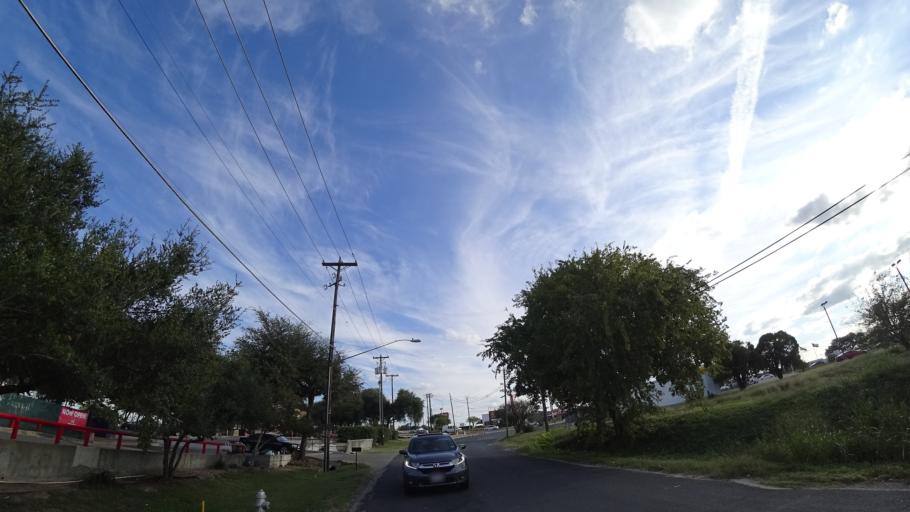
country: US
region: Texas
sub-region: Travis County
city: Onion Creek
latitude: 30.1919
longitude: -97.7715
